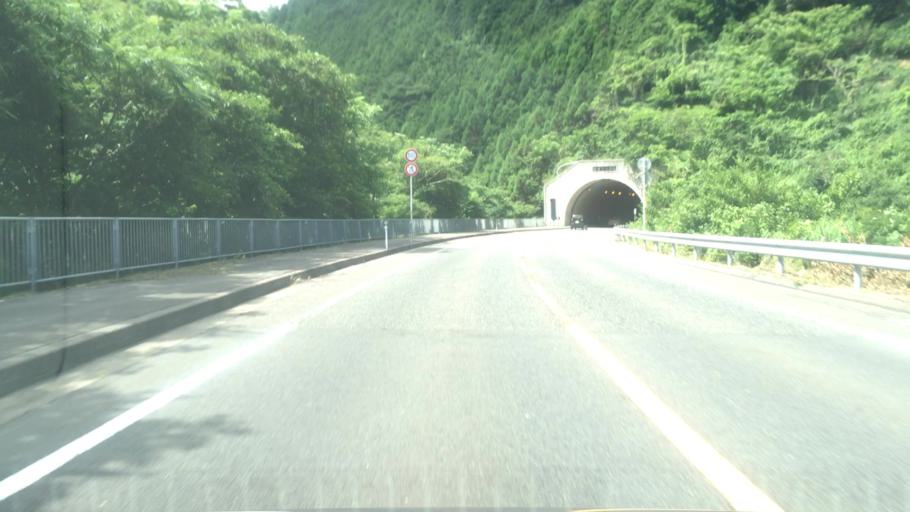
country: JP
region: Tottori
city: Tottori
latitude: 35.6178
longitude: 134.4160
